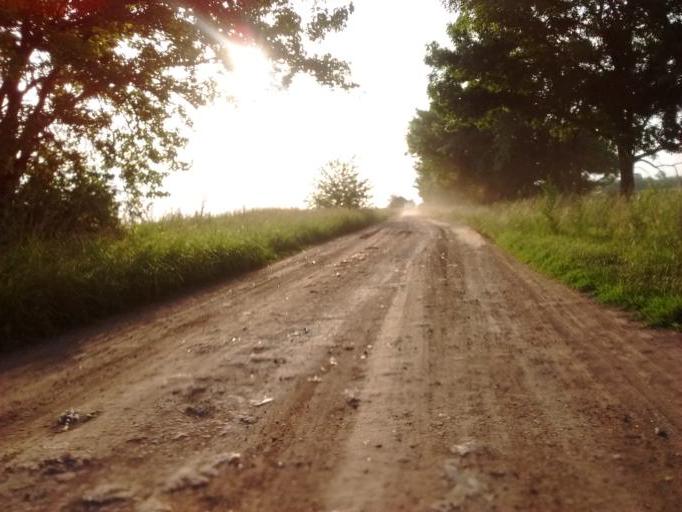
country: AR
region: Santa Fe
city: Funes
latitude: -32.9307
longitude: -60.8577
